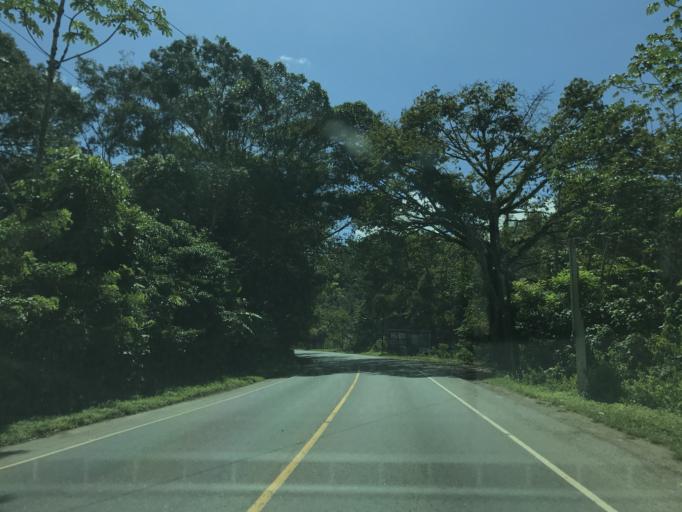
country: GT
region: Izabal
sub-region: Municipio de Puerto Barrios
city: Puerto Barrios
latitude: 15.6647
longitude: -88.5583
